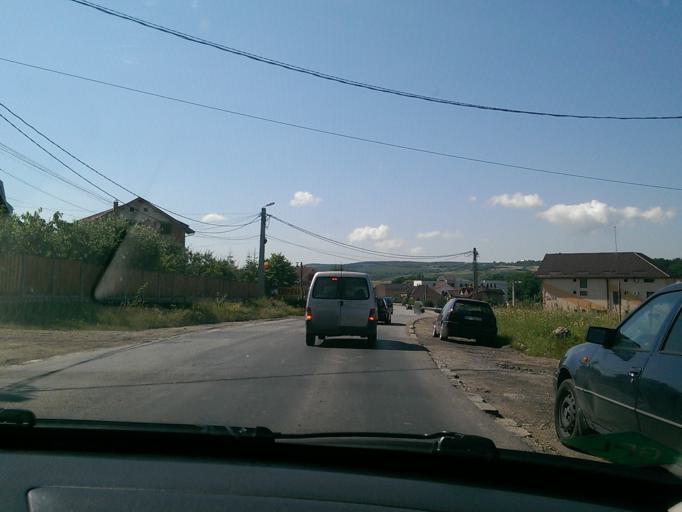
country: RO
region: Bihor
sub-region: Comuna Sanmartin
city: Sanmartin
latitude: 46.9869
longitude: 21.9854
